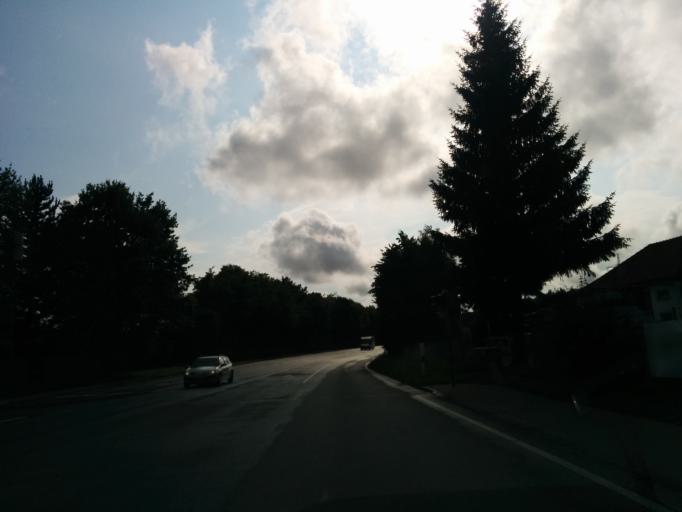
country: DE
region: Lower Saxony
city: Herzberg am Harz
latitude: 51.6506
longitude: 10.3328
